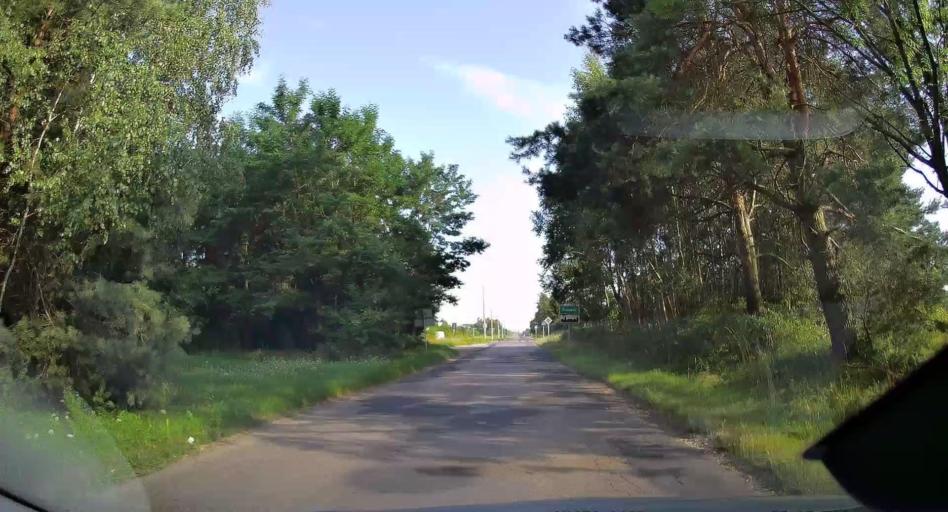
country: PL
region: Swietokrzyskie
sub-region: Powiat konecki
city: Konskie
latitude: 51.2184
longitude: 20.3900
